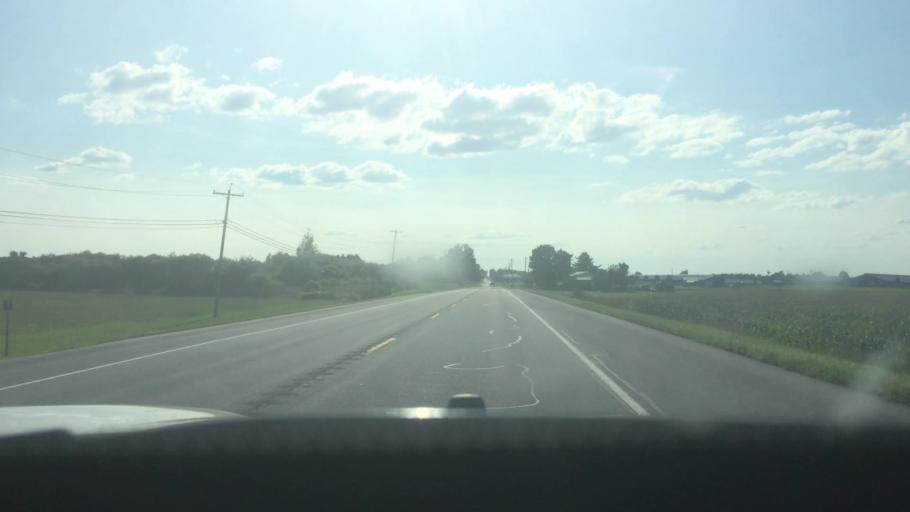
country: US
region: New York
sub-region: St. Lawrence County
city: Hannawa Falls
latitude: 44.6932
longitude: -74.6685
